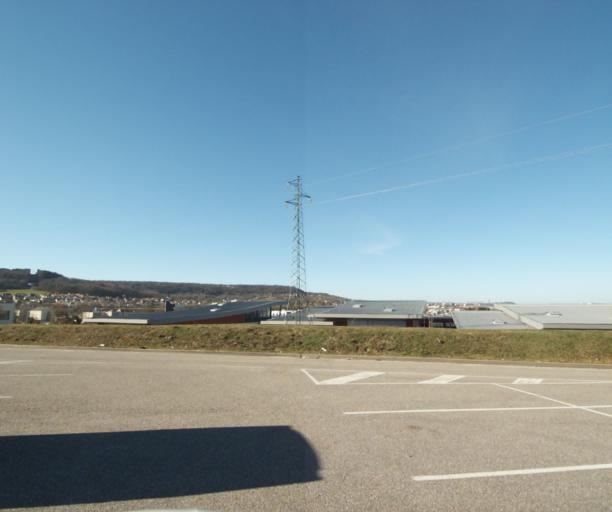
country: FR
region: Lorraine
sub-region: Departement de Meurthe-et-Moselle
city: Vandoeuvre-les-Nancy
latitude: 48.6380
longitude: 6.1895
